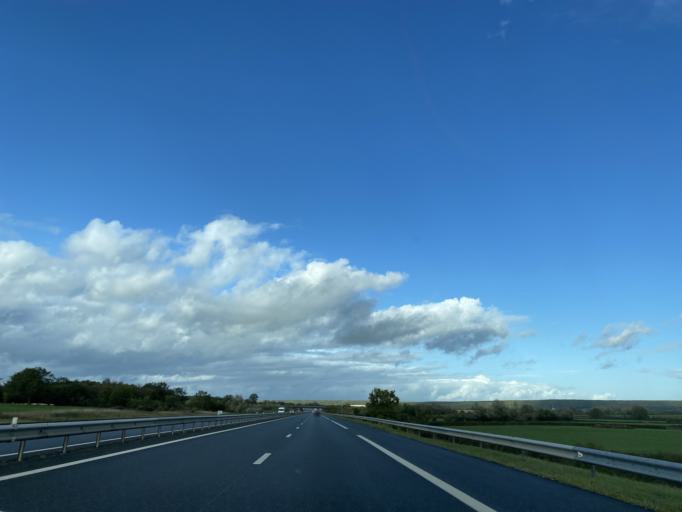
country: FR
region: Centre
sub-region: Departement du Cher
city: Orval
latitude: 46.7012
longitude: 2.4627
